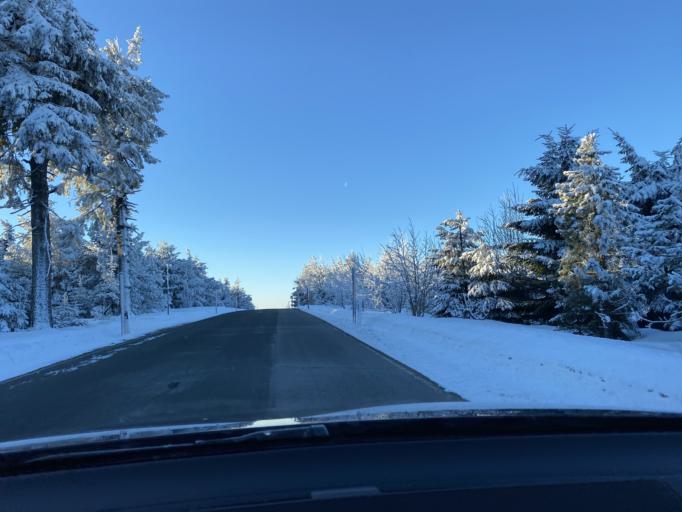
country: DE
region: Saxony
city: Kurort Oberwiesenthal
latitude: 50.4177
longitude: 12.9370
